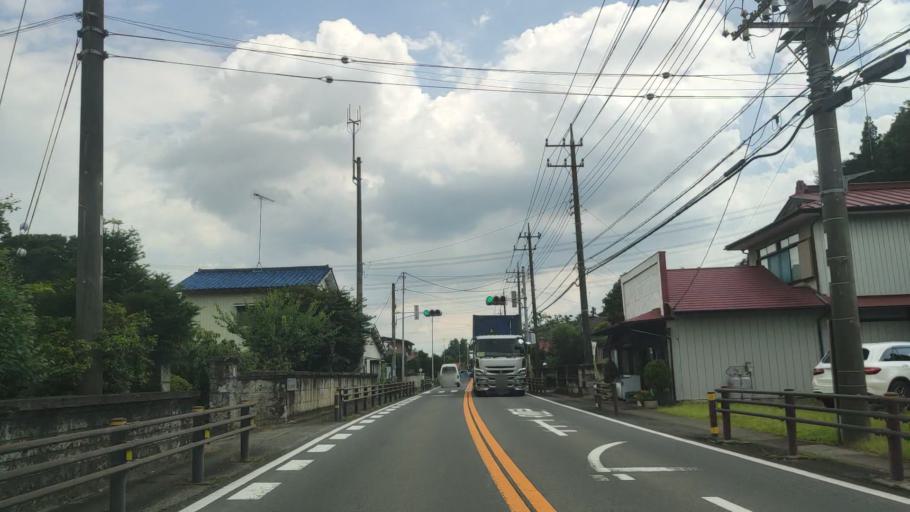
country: JP
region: Tochigi
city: Utsunomiya-shi
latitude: 36.6651
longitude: 139.8343
